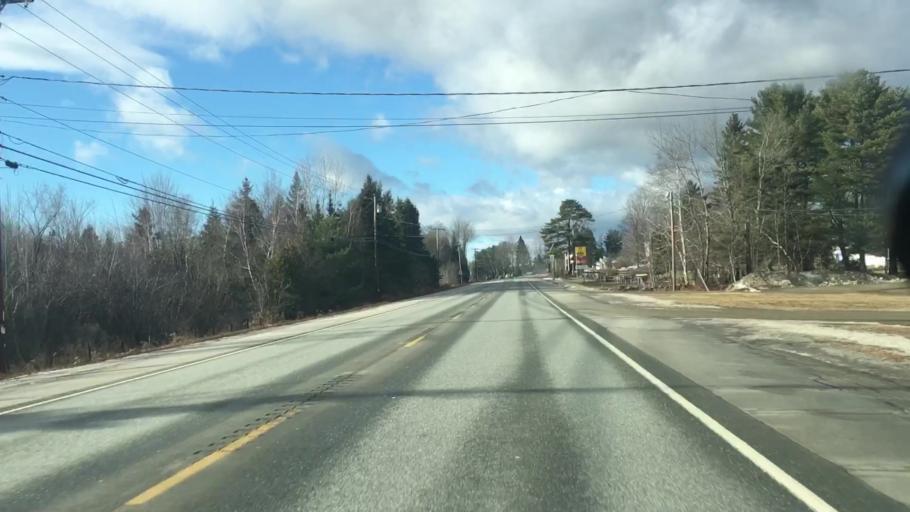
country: US
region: Maine
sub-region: Penobscot County
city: Holden
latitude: 44.7535
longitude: -68.6581
